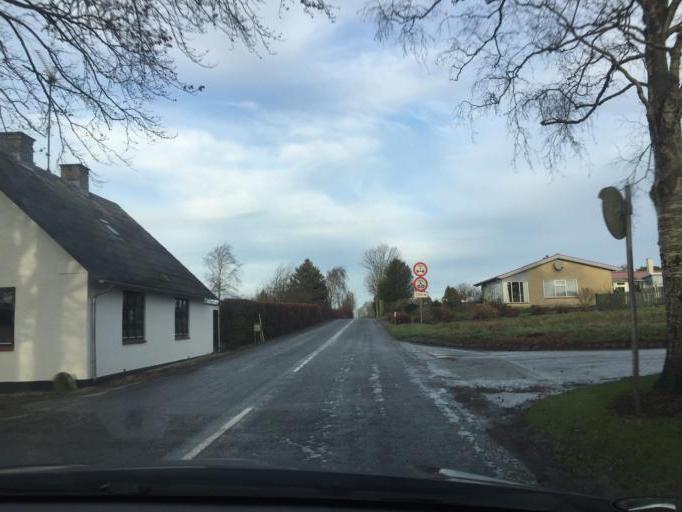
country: DK
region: South Denmark
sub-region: Faaborg-Midtfyn Kommune
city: Ringe
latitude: 55.1758
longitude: 10.4047
